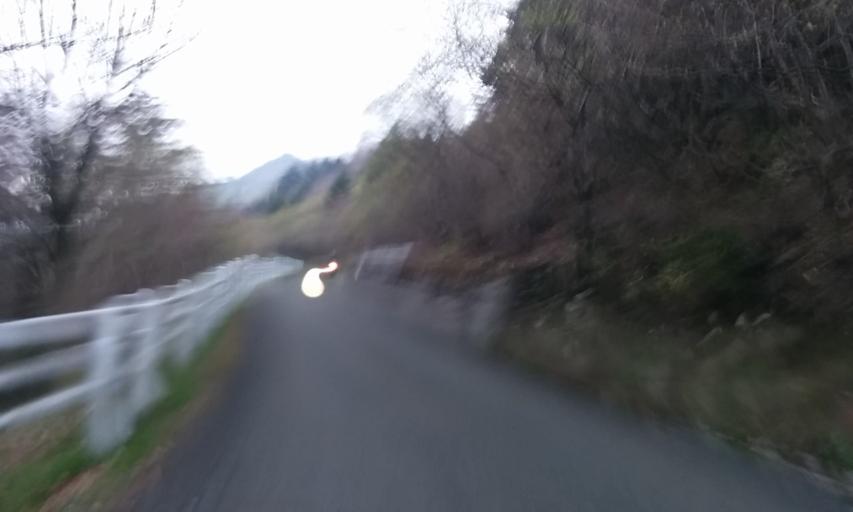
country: JP
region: Ehime
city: Saijo
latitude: 33.7856
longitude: 133.2147
